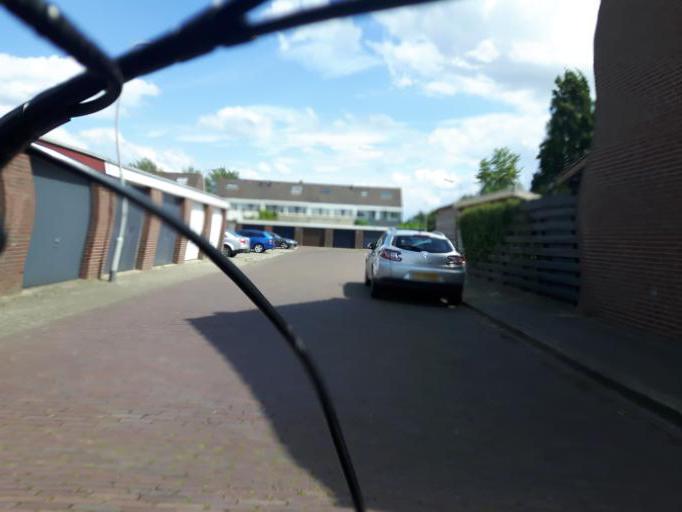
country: NL
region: Zeeland
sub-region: Gemeente Goes
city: Goes
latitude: 51.5068
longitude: 3.9057
